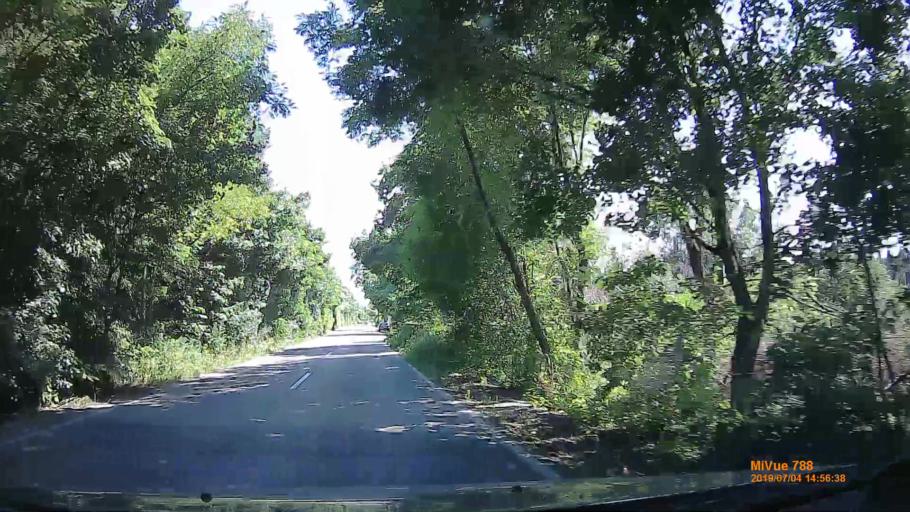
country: HU
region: Komarom-Esztergom
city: Tatabanya
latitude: 47.5453
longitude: 18.3808
